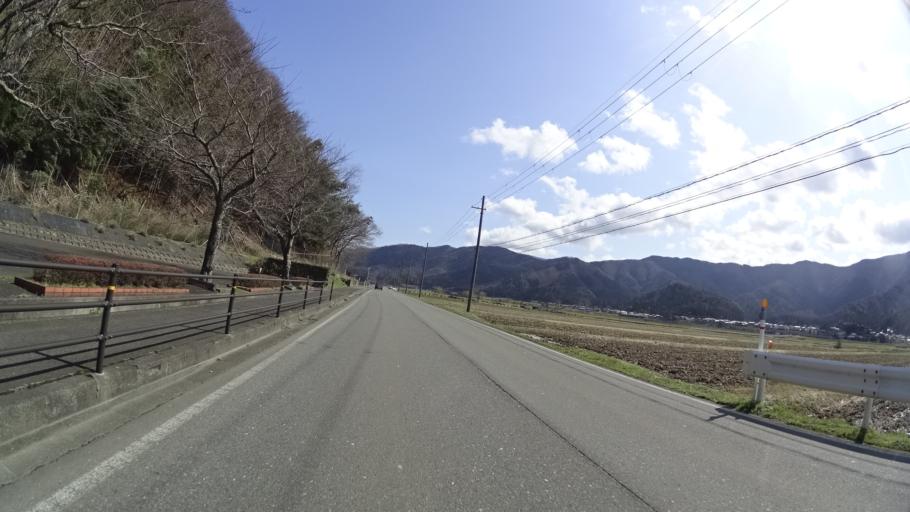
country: JP
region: Fukui
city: Obama
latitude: 35.4639
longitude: 135.8711
